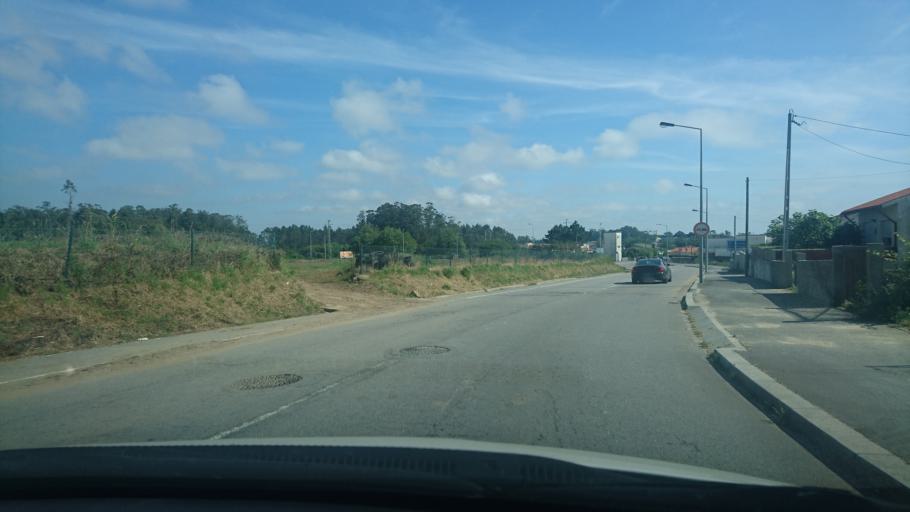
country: PT
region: Porto
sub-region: Matosinhos
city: Lavra
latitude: 41.2614
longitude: -8.7075
